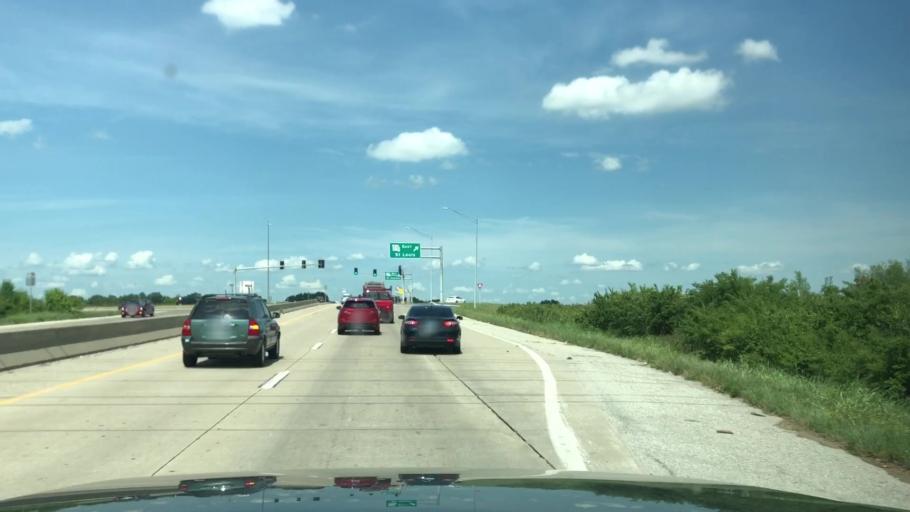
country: US
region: Missouri
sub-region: Saint Charles County
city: Saint Charles
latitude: 38.7904
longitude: -90.4541
